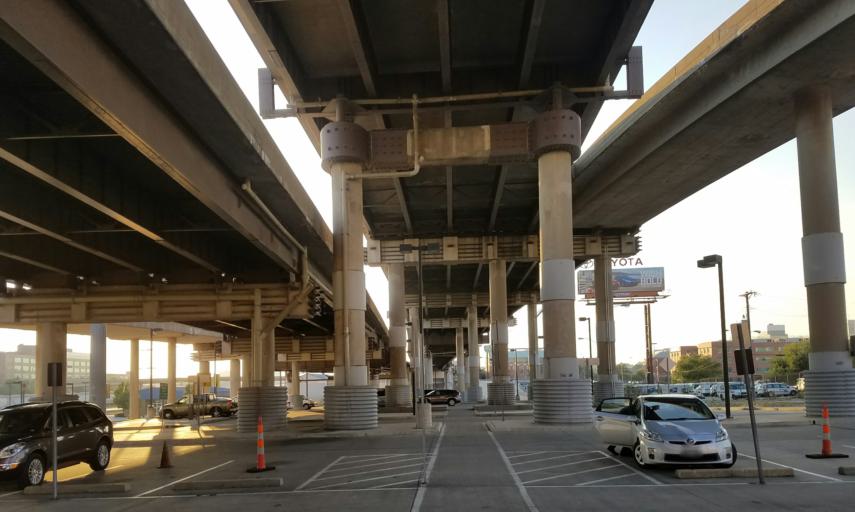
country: US
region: Missouri
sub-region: City of Saint Louis
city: St. Louis
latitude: 38.6243
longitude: -90.2038
